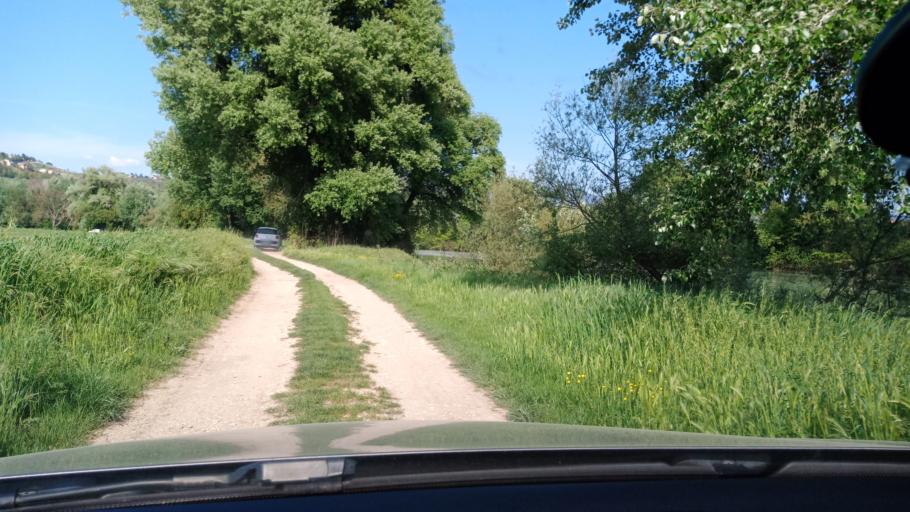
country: IT
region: Latium
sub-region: Provincia di Rieti
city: Forano
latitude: 42.2794
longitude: 12.5825
